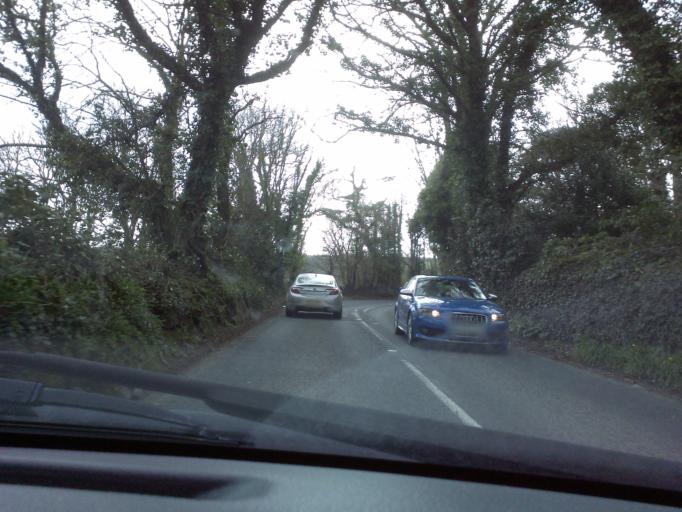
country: GB
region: England
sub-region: Cornwall
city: Penzance
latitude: 50.1082
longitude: -5.5682
